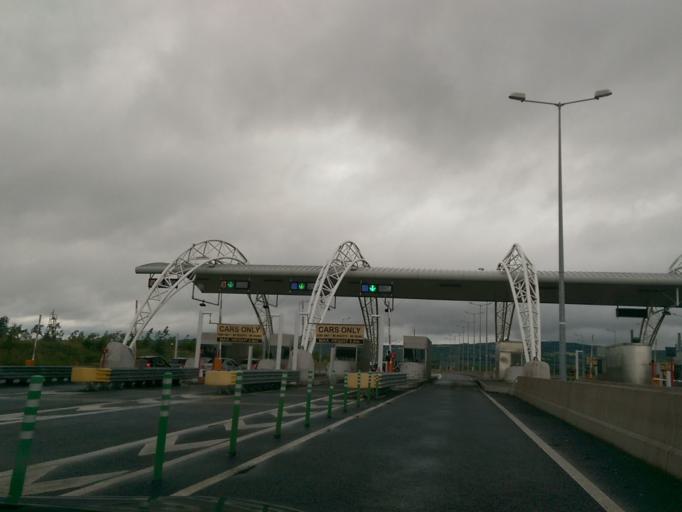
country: IE
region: Munster
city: Moyross
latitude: 52.6691
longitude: -8.6999
